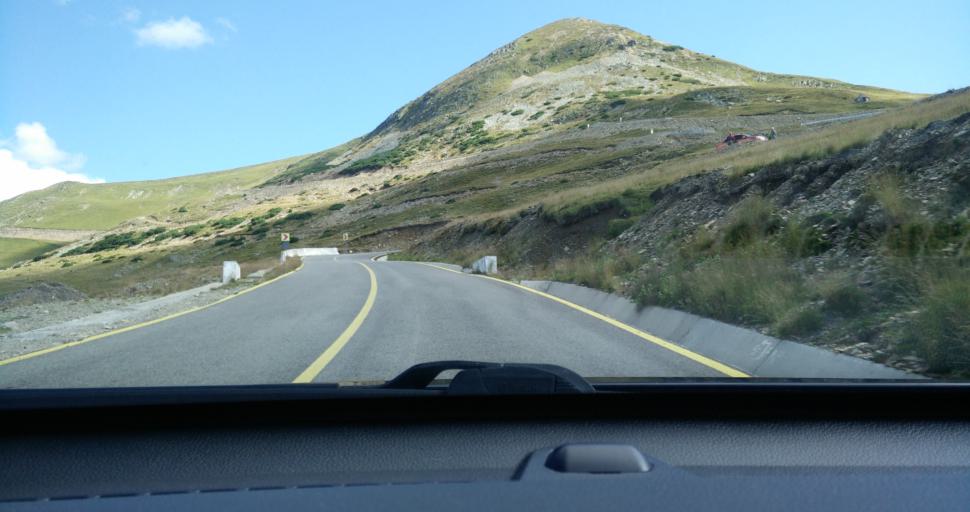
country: RO
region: Gorj
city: Novaci-Straini
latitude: 45.3185
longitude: 23.6819
